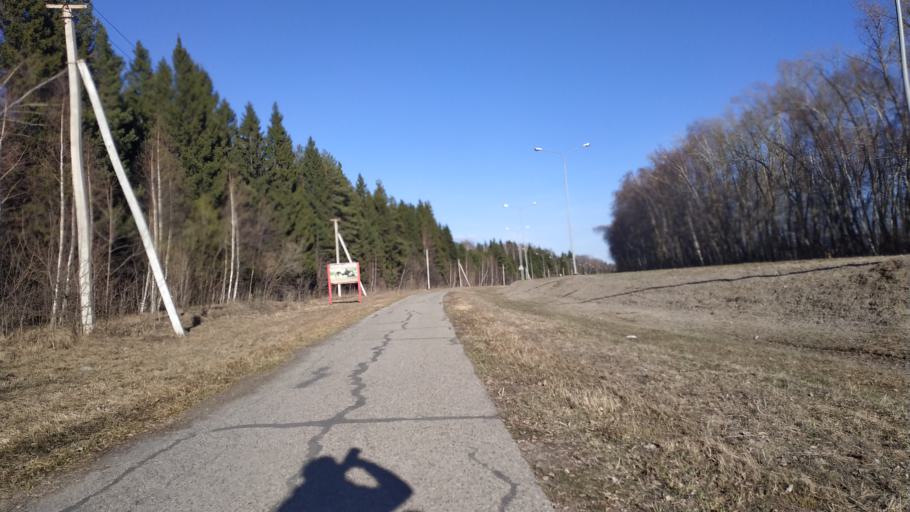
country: RU
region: Chuvashia
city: Ishley
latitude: 56.1350
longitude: 47.0931
